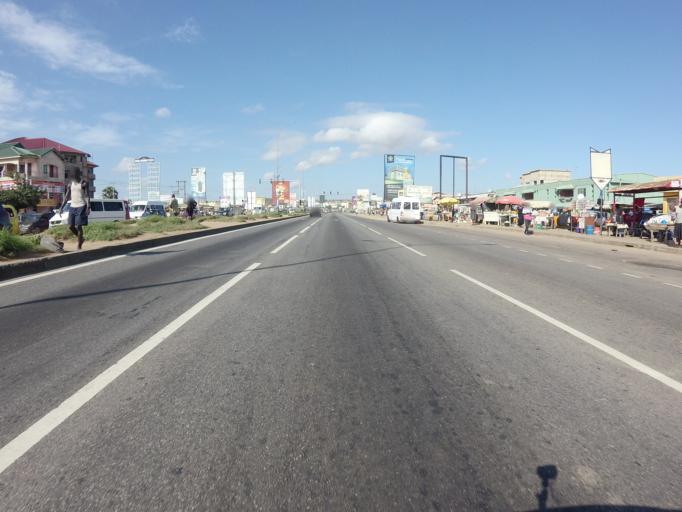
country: GH
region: Greater Accra
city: Gbawe
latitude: 5.5475
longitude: -0.3386
